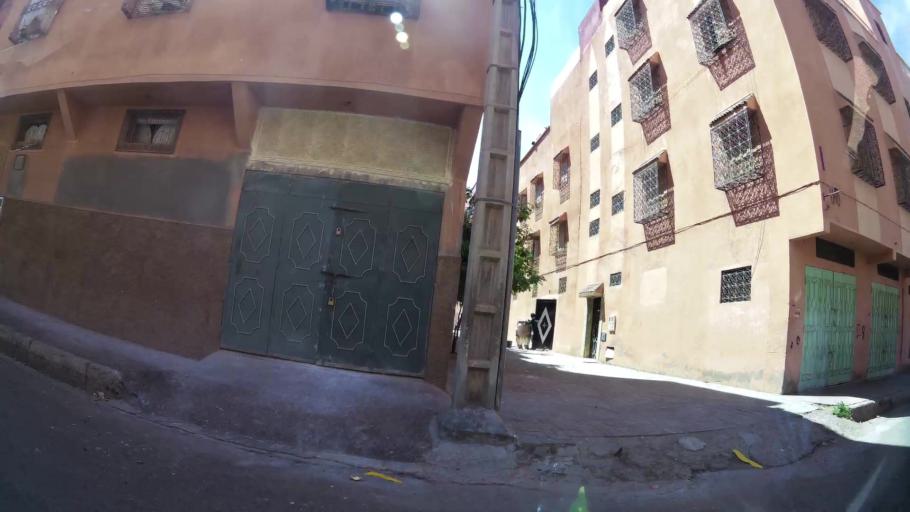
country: MA
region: Marrakech-Tensift-Al Haouz
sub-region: Marrakech
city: Marrakesh
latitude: 31.6425
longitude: -8.0664
